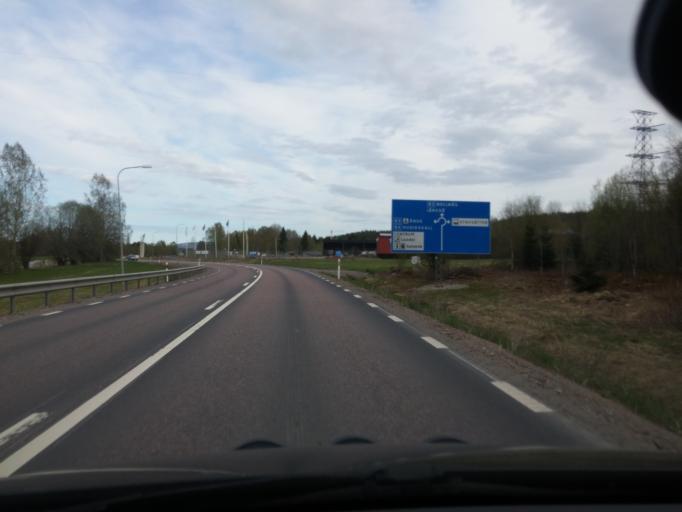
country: SE
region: Gaevleborg
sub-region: Ljusdals Kommun
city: Ljusdal
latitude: 61.8219
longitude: 16.0554
